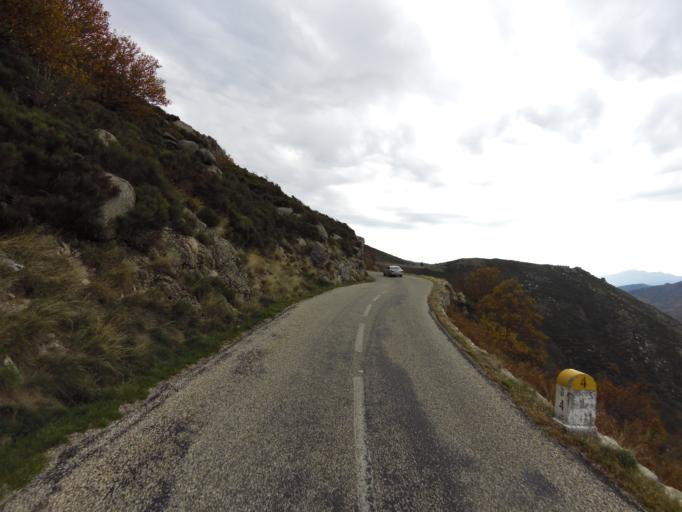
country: FR
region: Rhone-Alpes
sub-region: Departement de l'Ardeche
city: Les Vans
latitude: 44.5180
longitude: 4.0248
